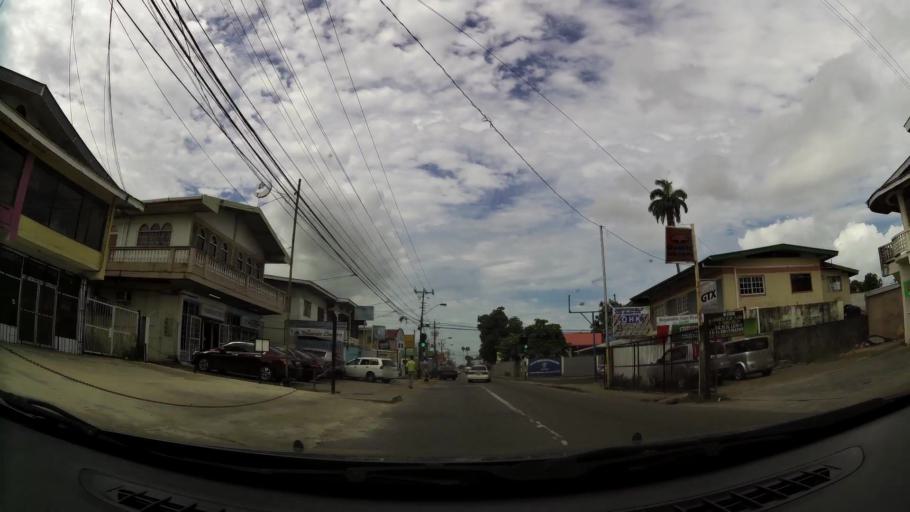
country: TT
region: Couva-Tabaquite-Talparo
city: Couva
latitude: 10.4223
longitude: -61.4665
